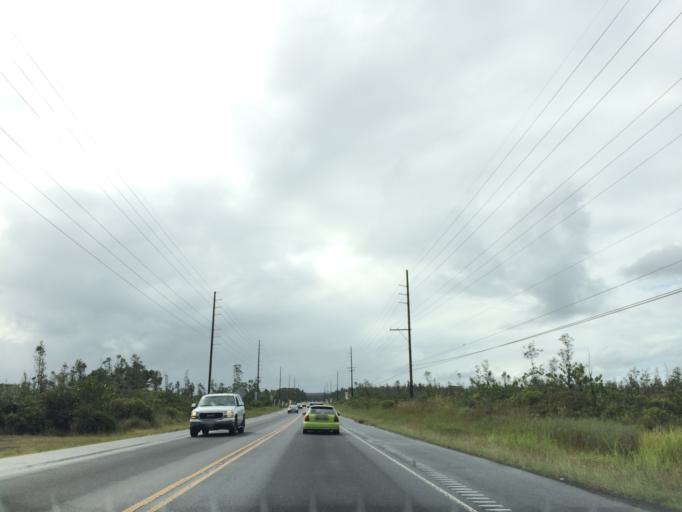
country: US
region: Hawaii
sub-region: Hawaii County
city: Ainaloa
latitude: 19.5406
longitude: -154.9734
